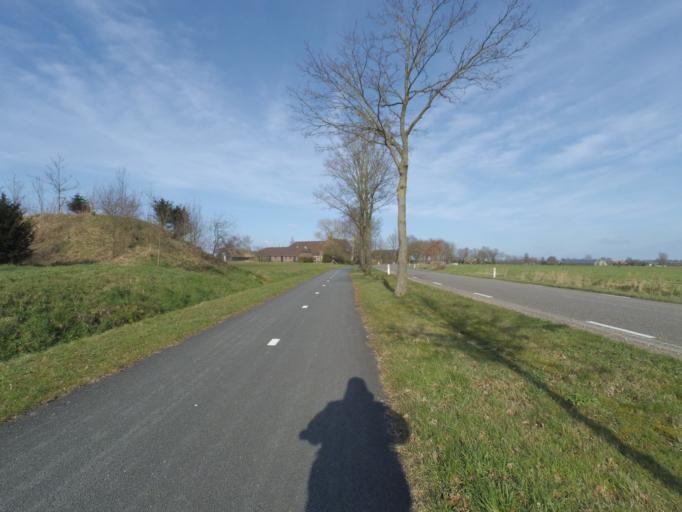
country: NL
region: Utrecht
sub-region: Gemeente Leusden
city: Leusden
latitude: 52.1496
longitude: 5.4237
